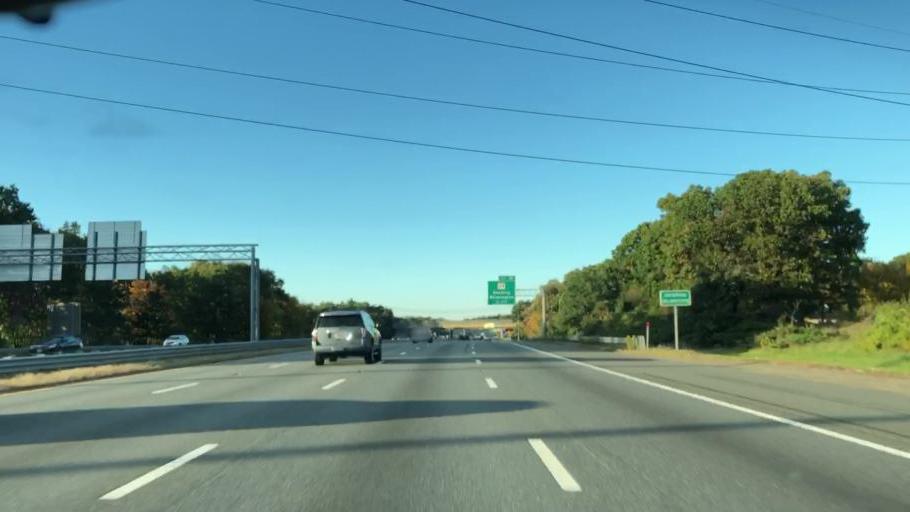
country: US
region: Massachusetts
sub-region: Middlesex County
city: Reading
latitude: 42.5296
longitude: -71.1358
